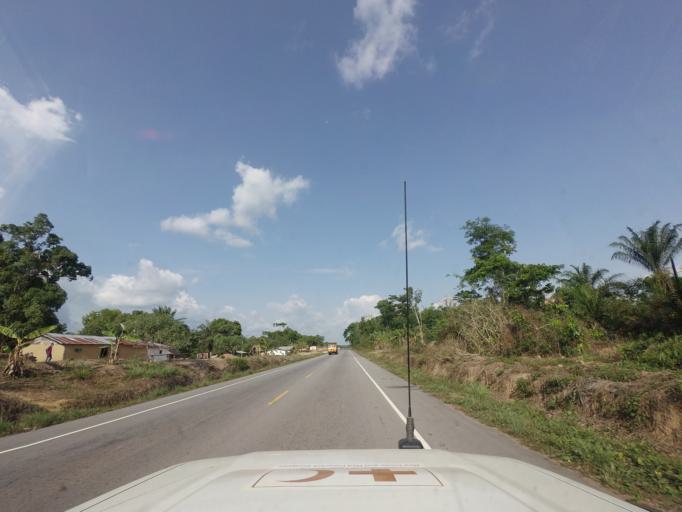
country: LR
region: Bong
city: Gbarnga
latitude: 6.8457
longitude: -9.8239
